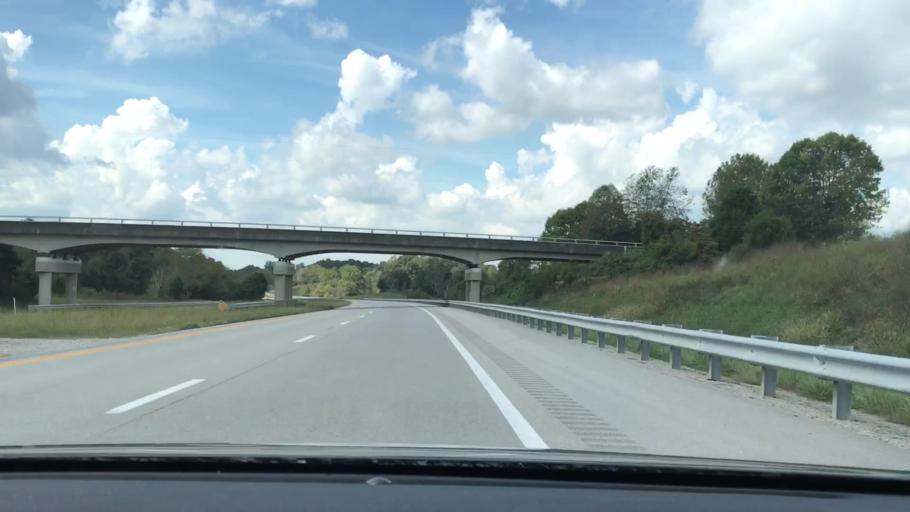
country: US
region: Kentucky
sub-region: Pulaski County
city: Somerset
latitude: 37.0973
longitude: -84.7225
